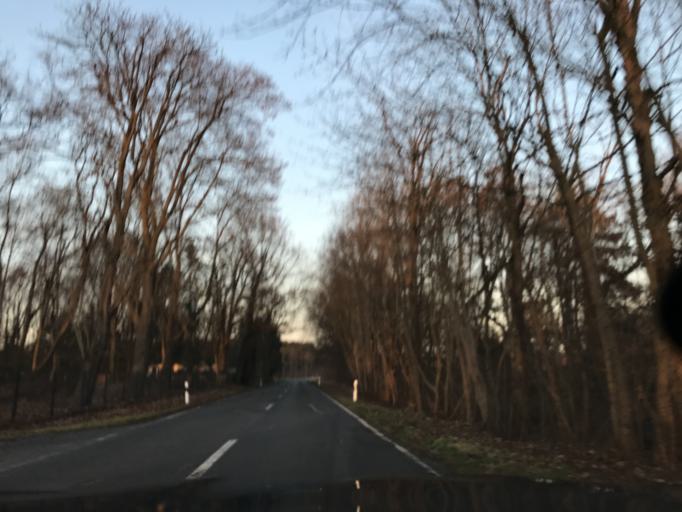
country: DE
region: Brandenburg
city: Wusterwitz
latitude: 52.4577
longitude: 12.4387
